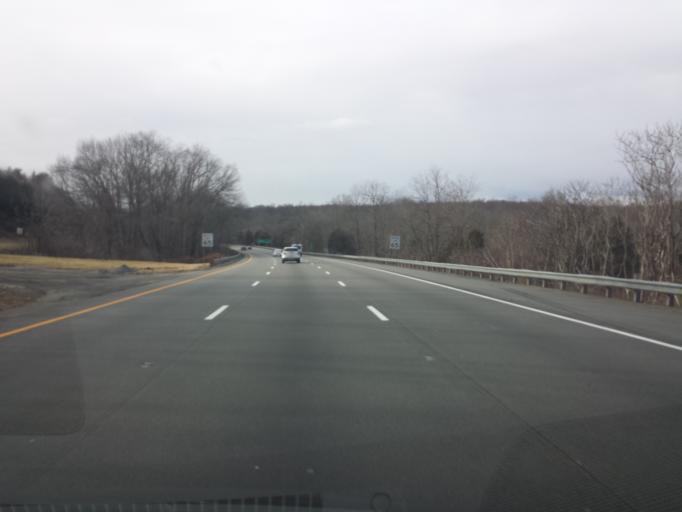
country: US
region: New Jersey
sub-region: Warren County
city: Oxford
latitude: 40.9287
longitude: -74.9683
